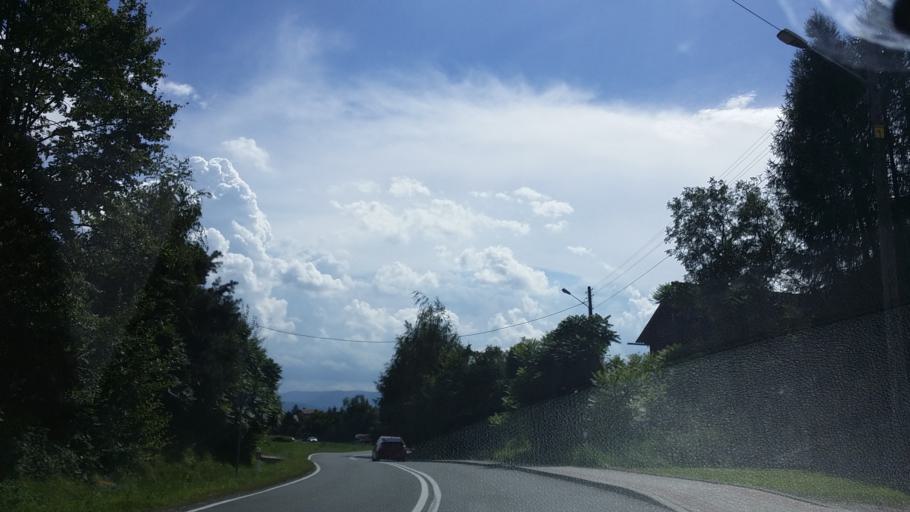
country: PL
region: Lesser Poland Voivodeship
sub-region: Powiat myslenicki
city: Dobczyce
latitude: 49.9078
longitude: 20.0979
